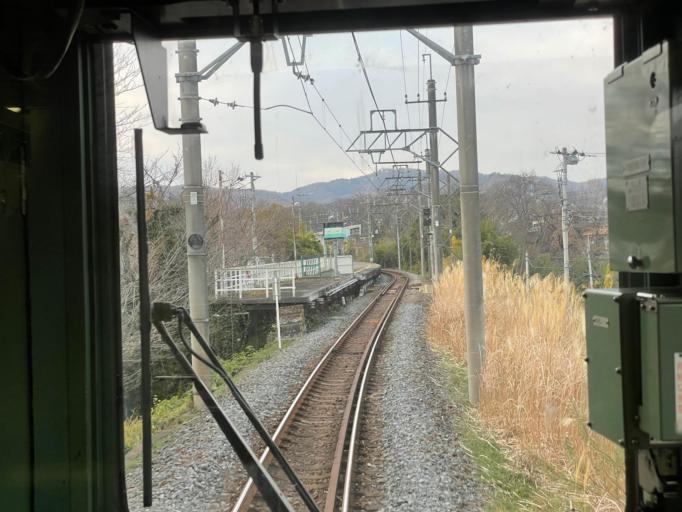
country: JP
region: Saitama
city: Yorii
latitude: 36.1162
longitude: 139.2014
